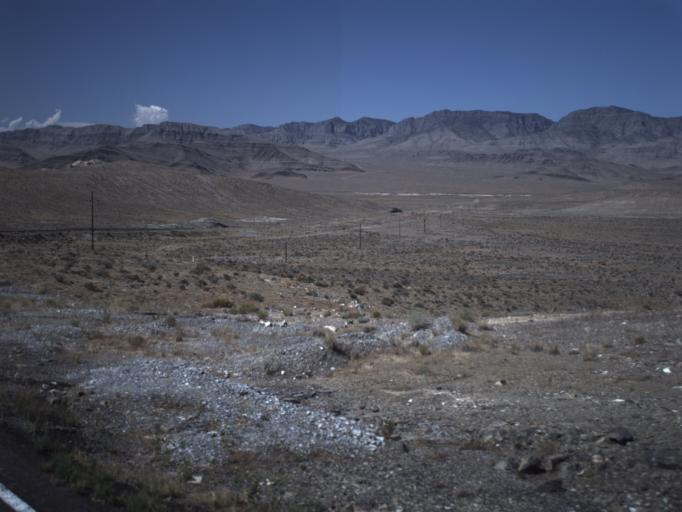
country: US
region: Utah
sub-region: Beaver County
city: Milford
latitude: 39.0299
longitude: -113.3430
